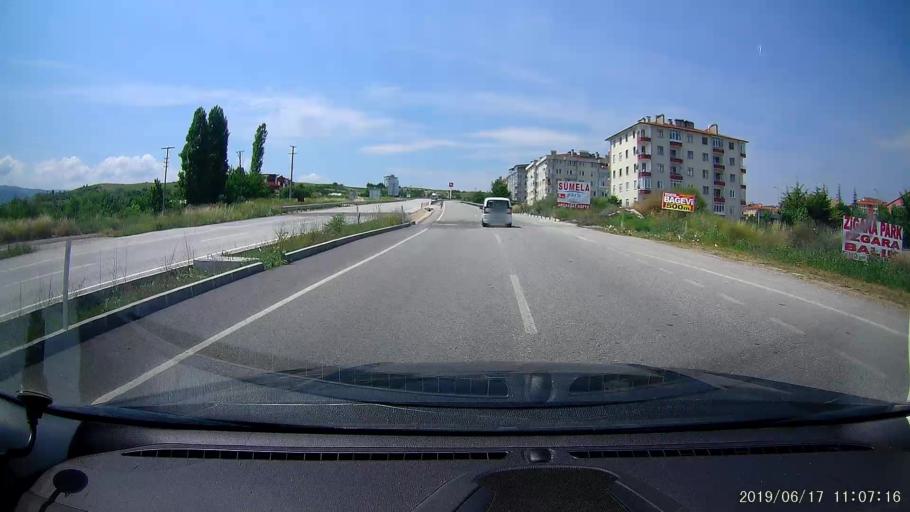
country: TR
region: Kastamonu
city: Tosya
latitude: 41.0049
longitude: 34.0562
